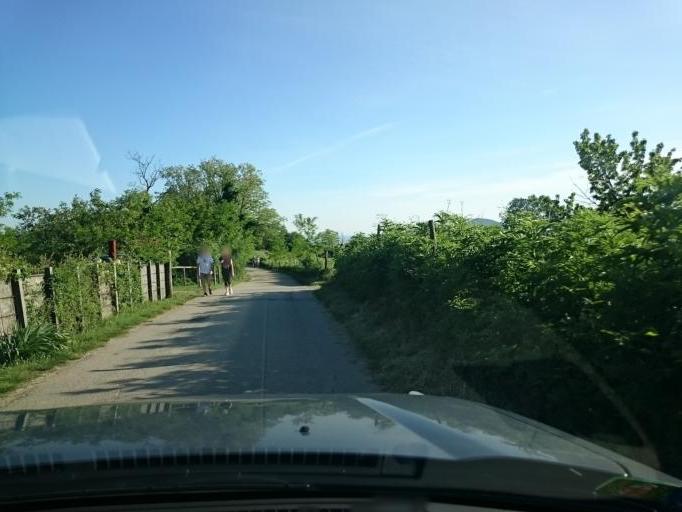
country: IT
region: Veneto
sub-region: Provincia di Padova
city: Arqua Petrarca
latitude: 45.2934
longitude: 11.7078
